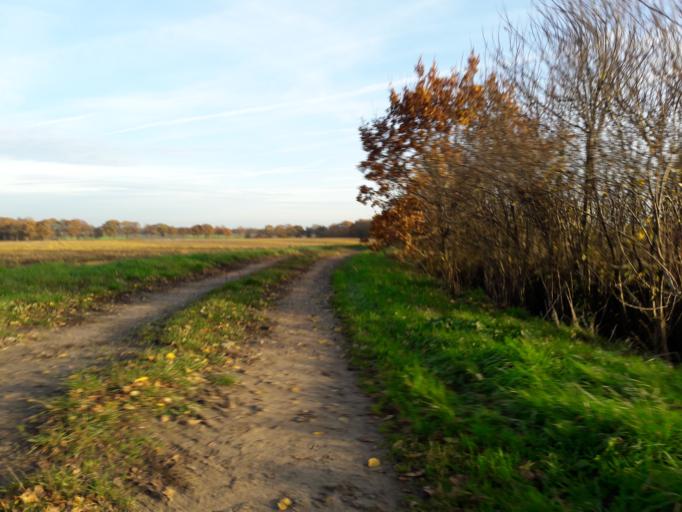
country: NL
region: Drenthe
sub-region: Gemeente Borger-Odoorn
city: Borger
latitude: 52.9561
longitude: 6.8164
